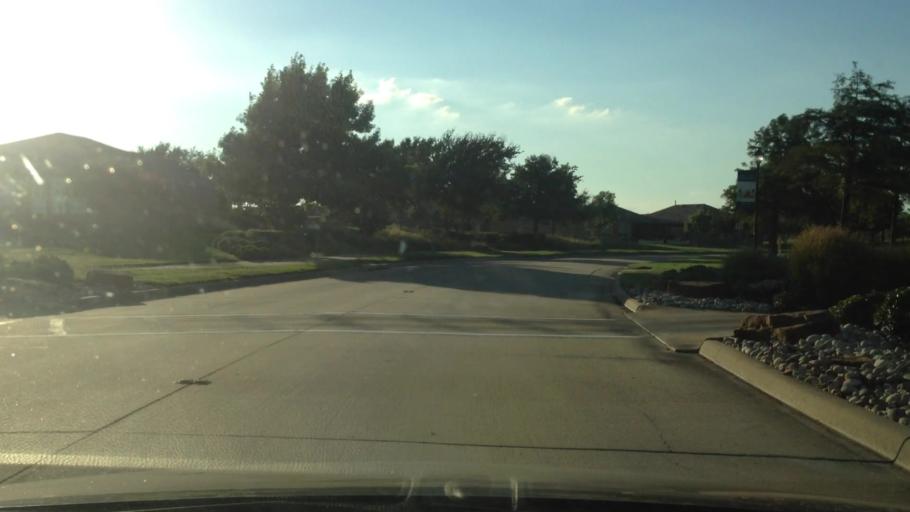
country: US
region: Texas
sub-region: Denton County
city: Little Elm
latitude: 33.1372
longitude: -96.8971
